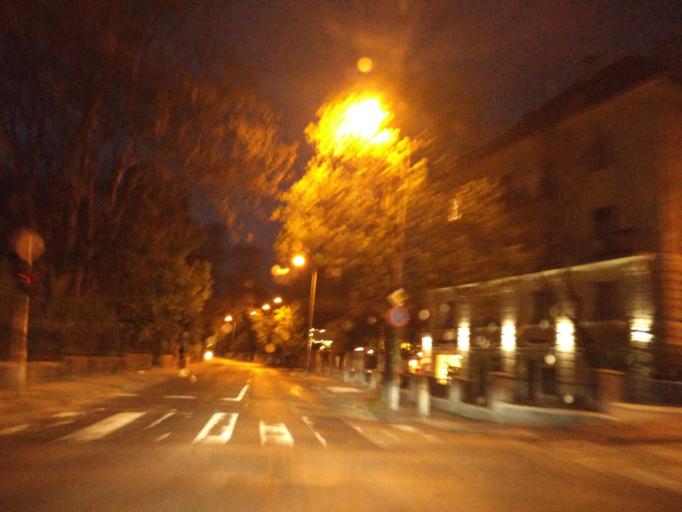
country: HU
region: Budapest
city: Budapest XII. keruelet
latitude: 47.5164
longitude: 19.0043
